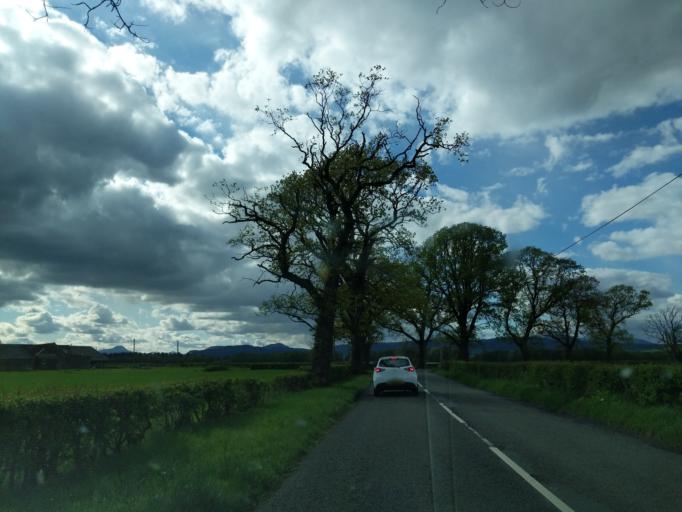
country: GB
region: Scotland
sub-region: Stirling
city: Callander
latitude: 56.1508
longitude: -4.1613
